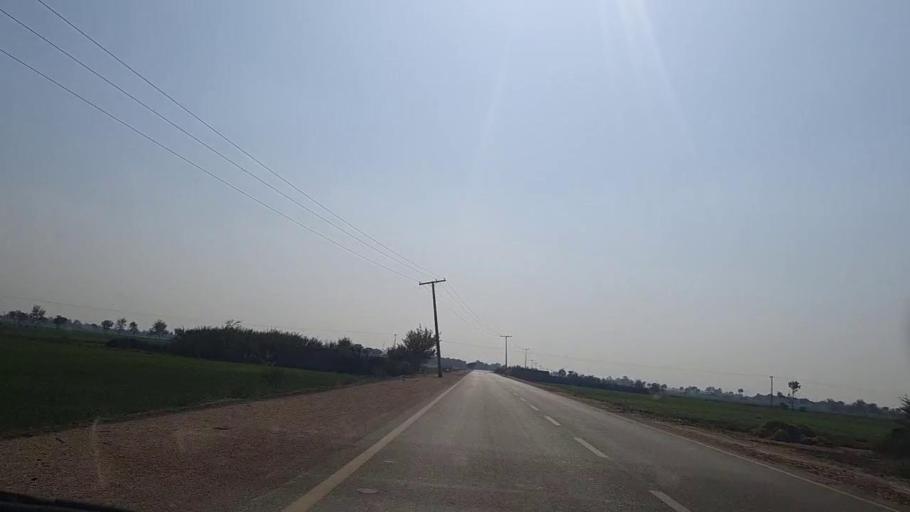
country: PK
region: Sindh
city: Sakrand
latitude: 26.0359
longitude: 68.4011
